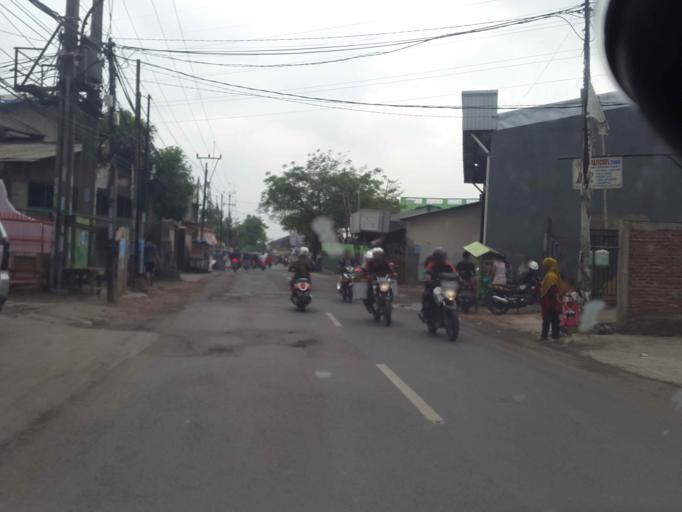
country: ID
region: West Java
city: Cikarang
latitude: -6.2733
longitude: 107.1499
